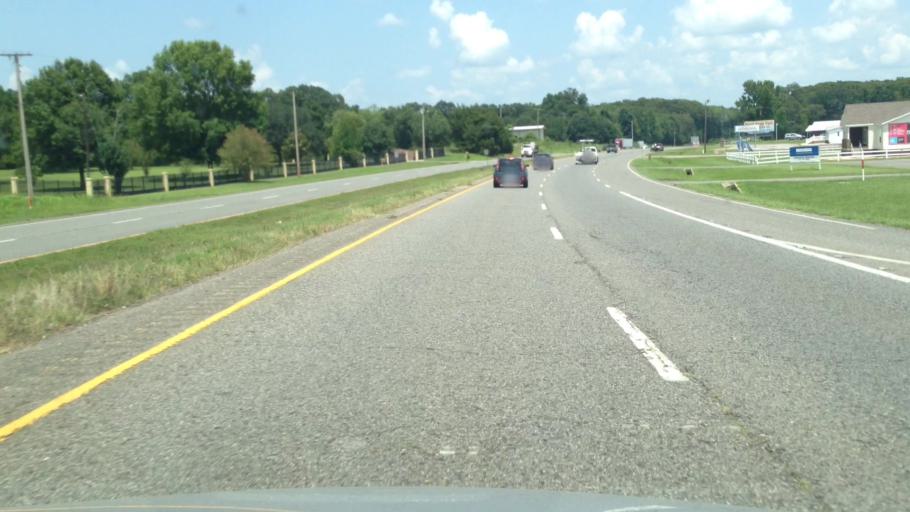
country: US
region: Louisiana
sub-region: Saint Landry Parish
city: Opelousas
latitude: 30.5369
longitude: -92.0566
